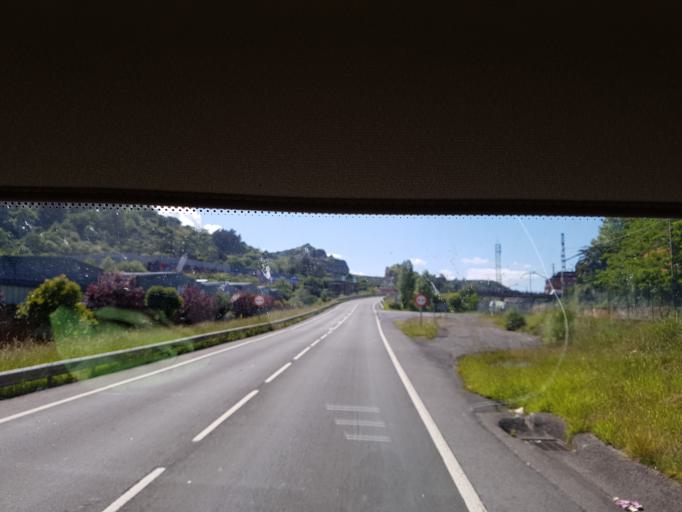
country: ES
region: Basque Country
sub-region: Bizkaia
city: Urtuella
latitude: 43.3063
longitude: -3.0485
